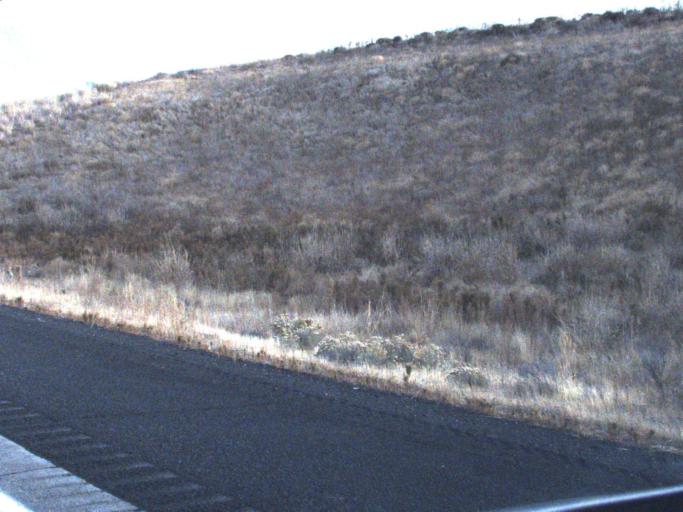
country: US
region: Washington
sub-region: Franklin County
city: Connell
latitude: 46.8702
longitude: -118.6303
